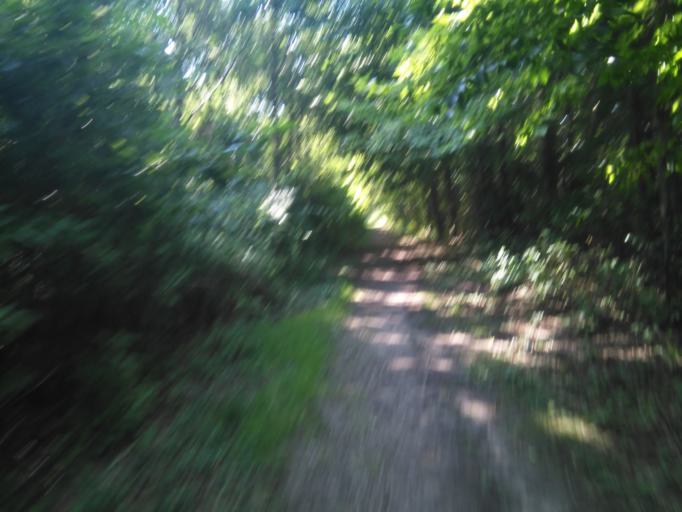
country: DK
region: Central Jutland
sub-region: Arhus Kommune
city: Stavtrup
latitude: 56.1507
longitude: 10.1395
